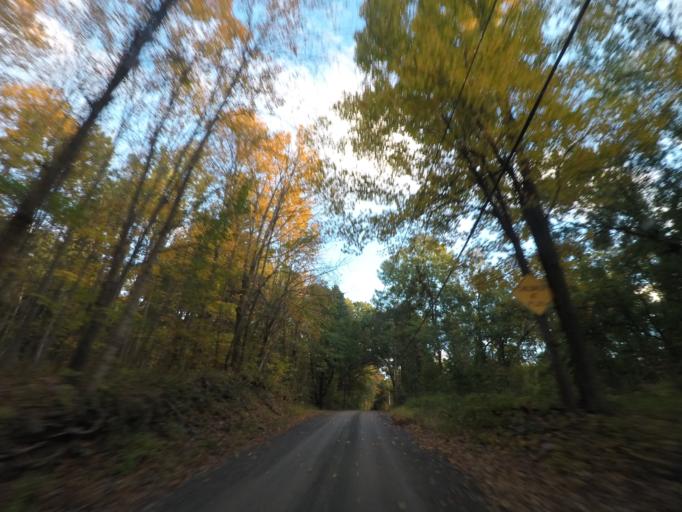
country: US
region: New York
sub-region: Rensselaer County
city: Nassau
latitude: 42.5150
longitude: -73.5916
